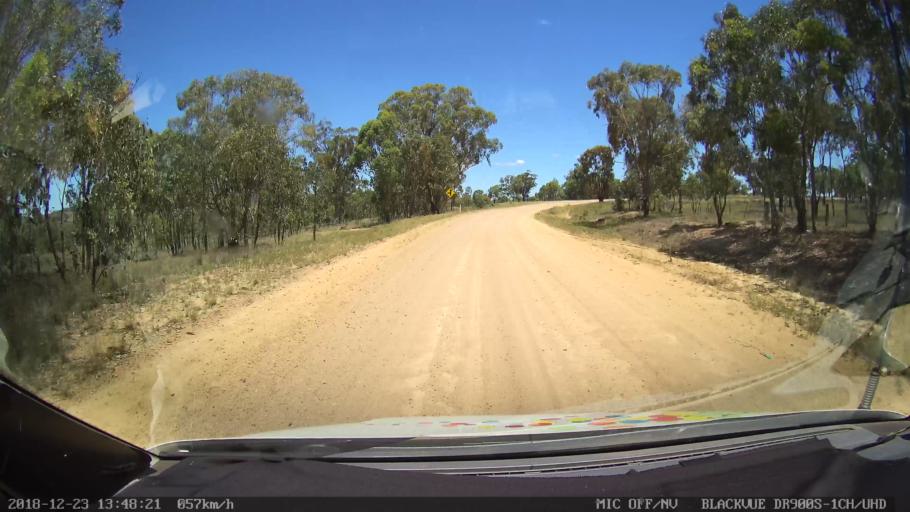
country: AU
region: New South Wales
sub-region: Tamworth Municipality
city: Manilla
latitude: -30.5168
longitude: 151.1167
